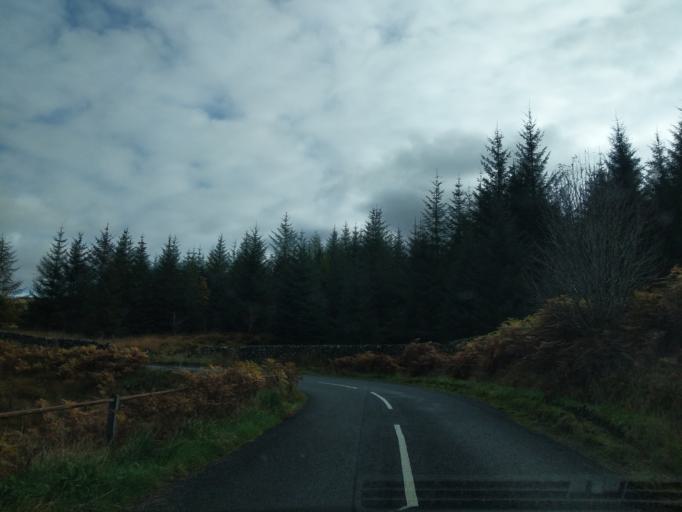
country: GB
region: Scotland
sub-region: Dumfries and Galloway
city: Castle Douglas
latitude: 55.1300
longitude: -4.0616
